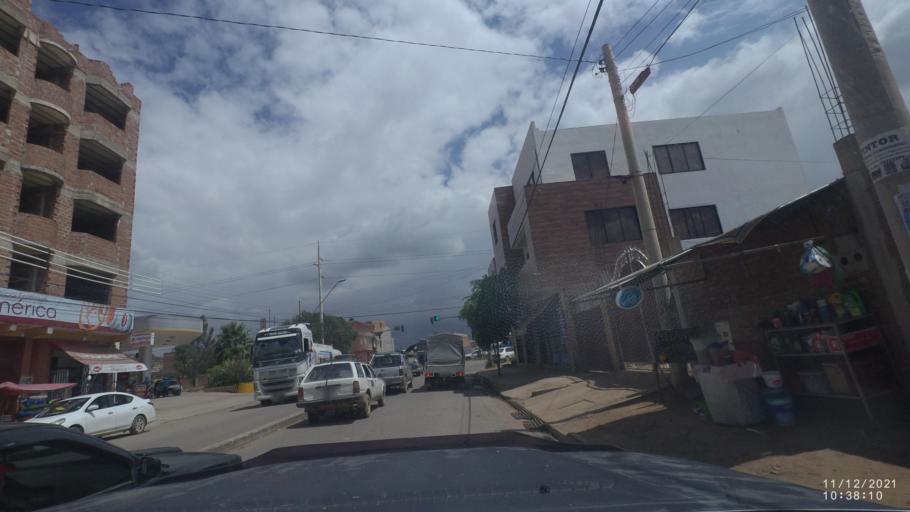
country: BO
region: Cochabamba
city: Cochabamba
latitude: -17.4405
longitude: -66.1250
